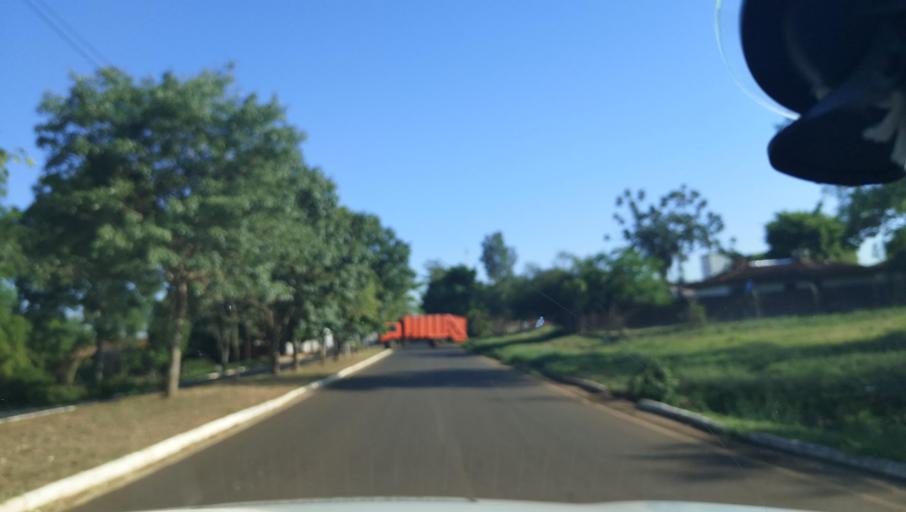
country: PY
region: Itapua
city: Carmen del Parana
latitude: -27.1579
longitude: -56.2424
